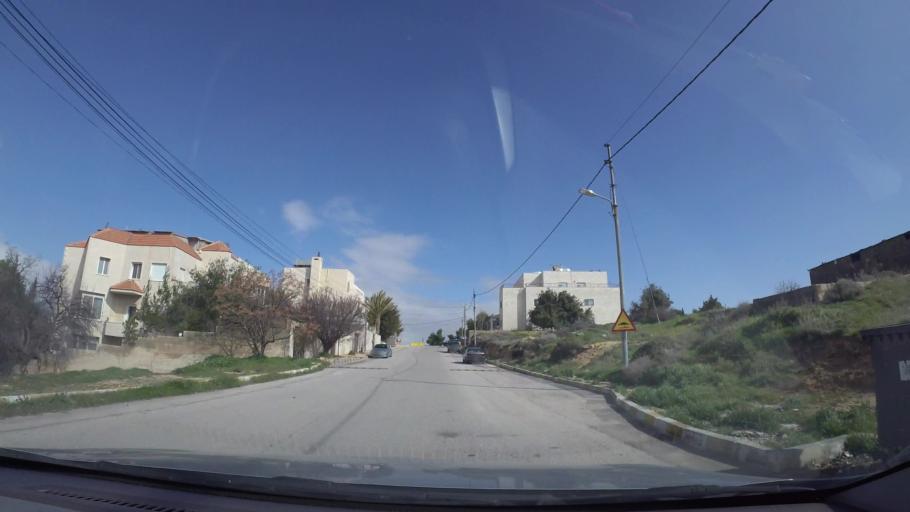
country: JO
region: Amman
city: Al Jubayhah
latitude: 32.0086
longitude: 35.8429
